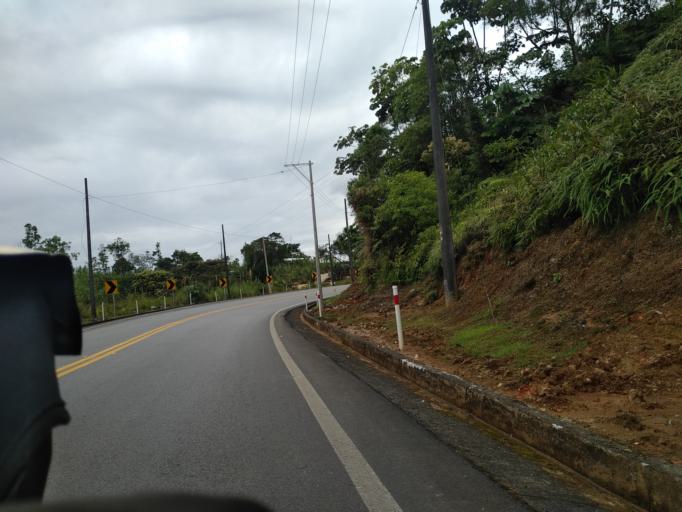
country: EC
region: Pastaza
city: Puyo
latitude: -1.3369
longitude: -77.9127
